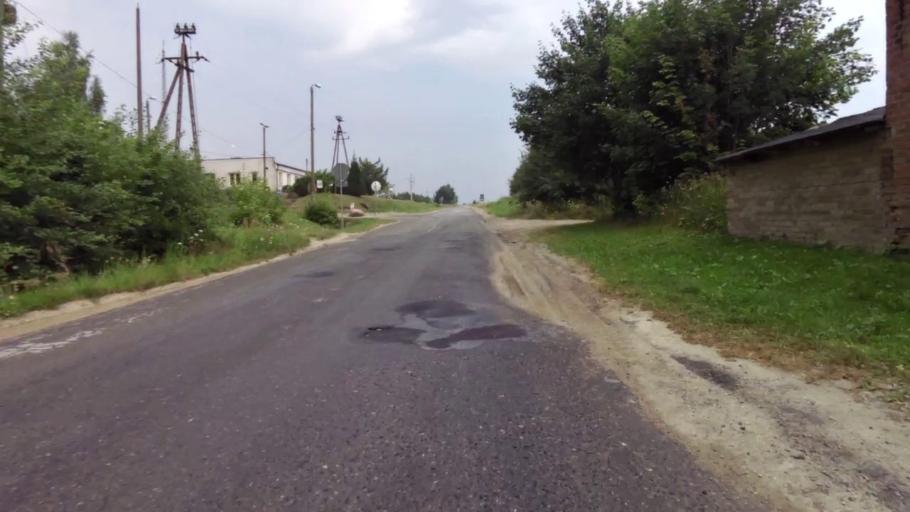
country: PL
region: West Pomeranian Voivodeship
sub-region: Powiat lobeski
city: Wegorzyno
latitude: 53.4884
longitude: 15.6193
